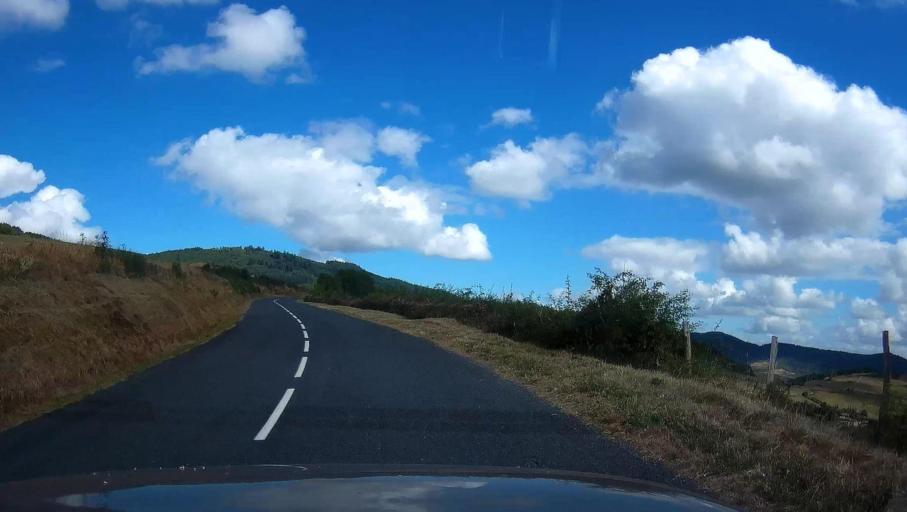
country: FR
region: Rhone-Alpes
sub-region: Departement du Rhone
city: Cogny
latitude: 45.9824
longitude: 4.5822
